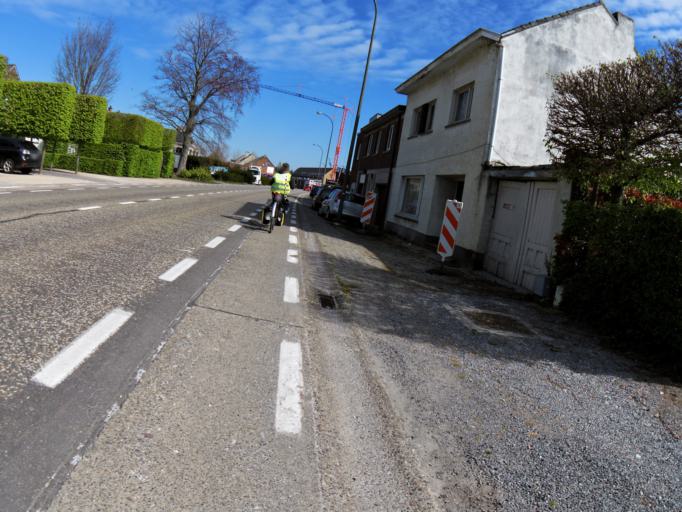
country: BE
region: Flanders
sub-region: Provincie Limburg
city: Zonhoven
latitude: 50.9844
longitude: 5.3669
